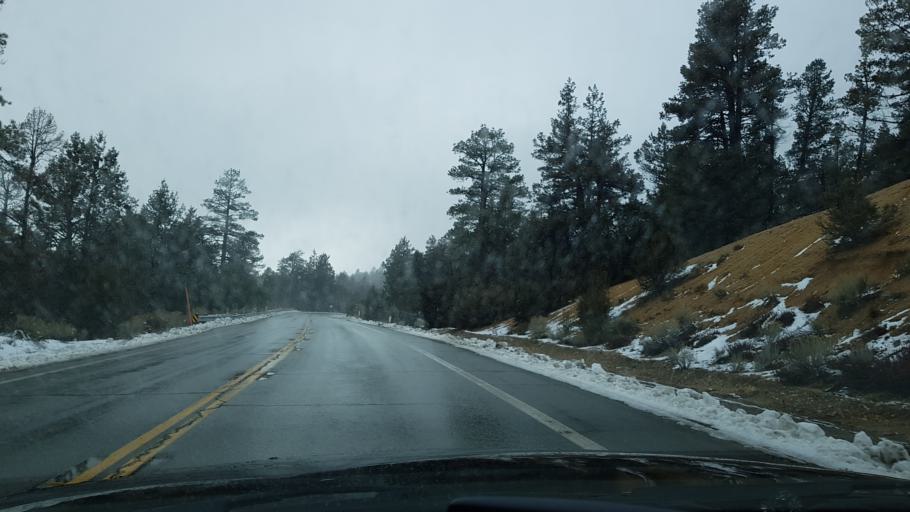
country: US
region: California
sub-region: San Bernardino County
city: Big Bear Lake
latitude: 34.2644
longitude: -116.9148
